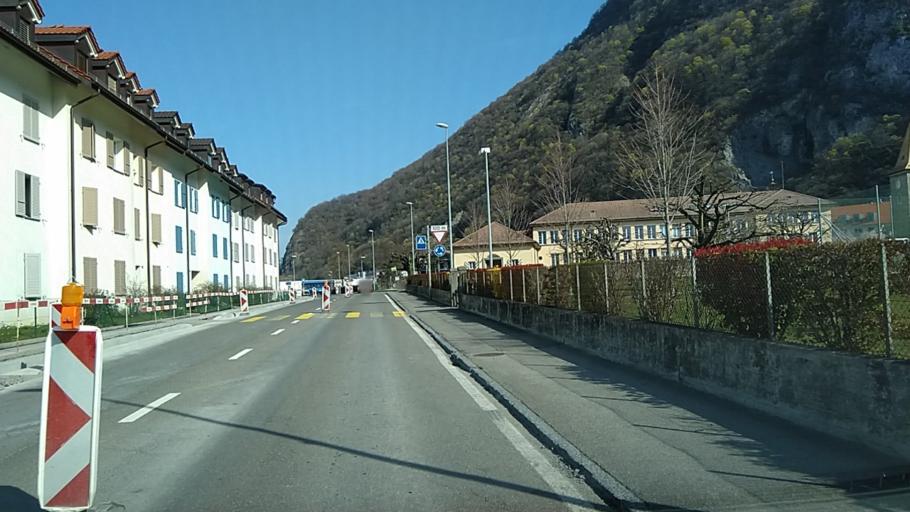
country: CH
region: Vaud
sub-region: Aigle District
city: Villeneuve
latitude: 46.3606
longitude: 6.9294
